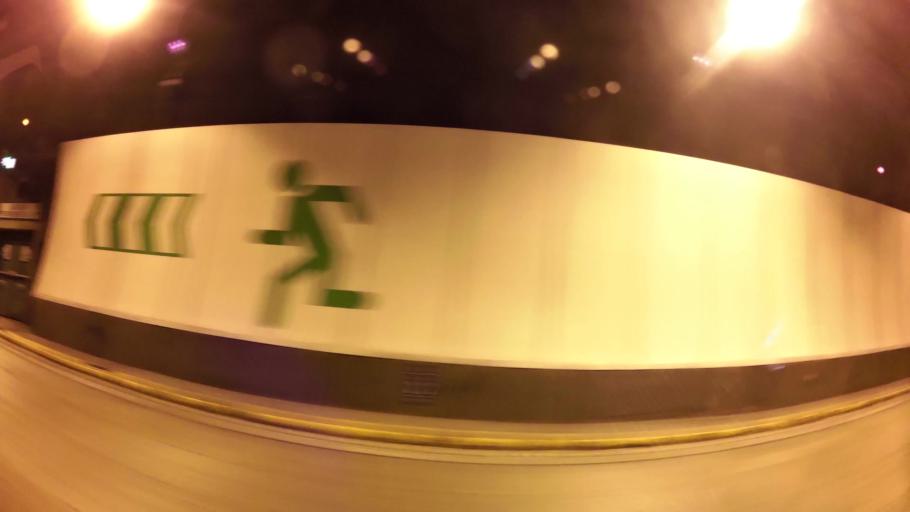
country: CL
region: Santiago Metropolitan
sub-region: Provincia de Santiago
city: Santiago
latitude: -33.4088
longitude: -70.6145
